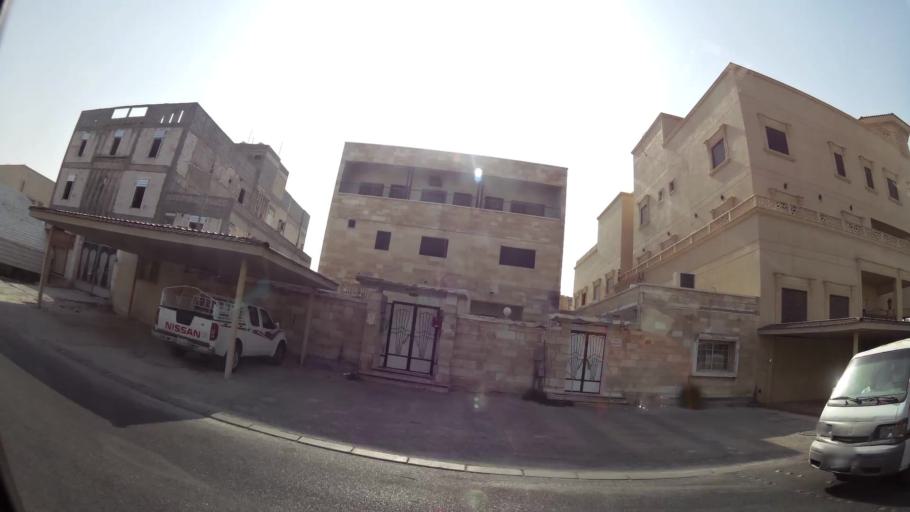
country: KW
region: Muhafazat al Jahra'
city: Al Jahra'
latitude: 29.3554
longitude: 47.6766
